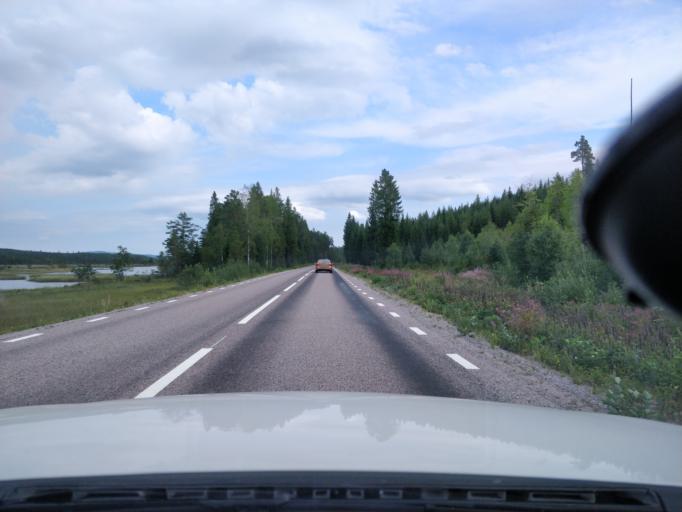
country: SE
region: Dalarna
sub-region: Ludvika Kommun
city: Abborrberget
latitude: 60.1911
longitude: 14.8243
